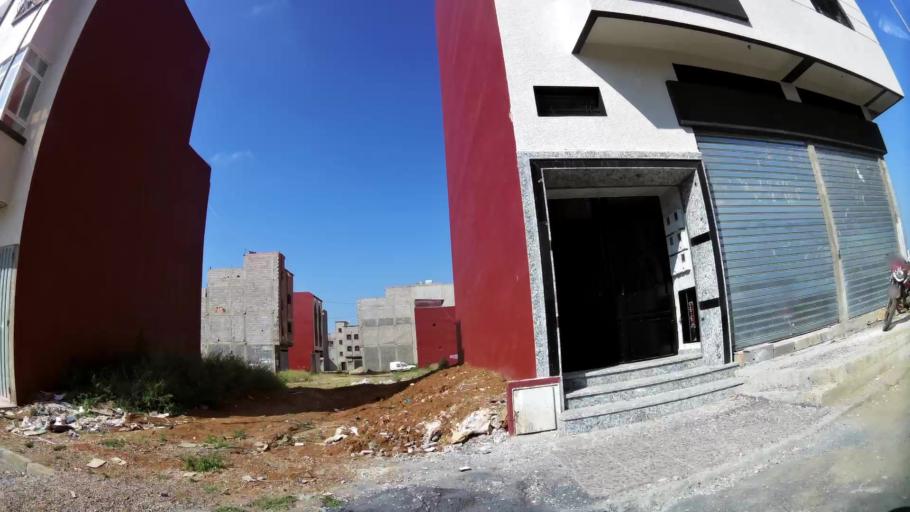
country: MA
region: Rabat-Sale-Zemmour-Zaer
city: Sale
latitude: 34.0614
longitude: -6.7672
